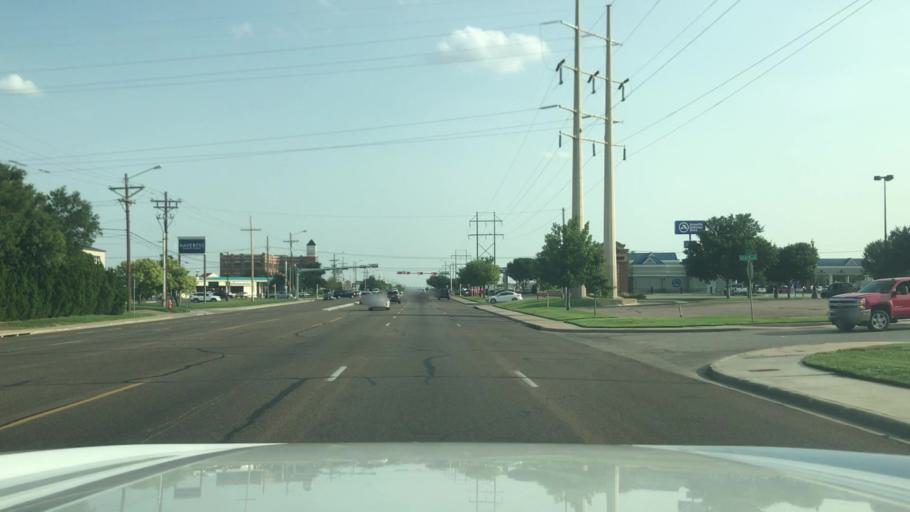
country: US
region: Texas
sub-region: Potter County
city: Amarillo
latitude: 35.1784
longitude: -101.9383
